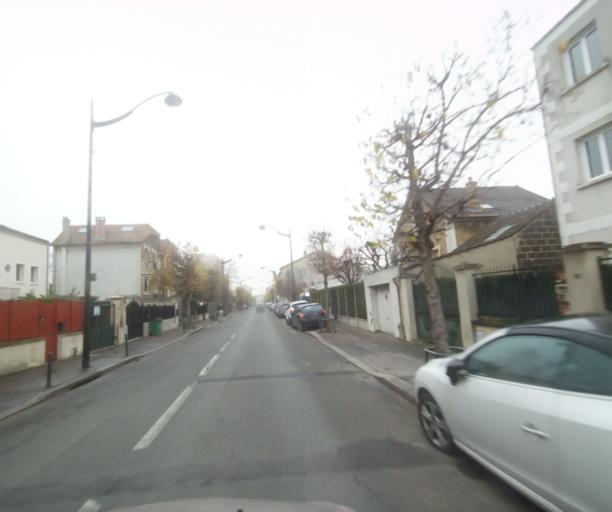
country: FR
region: Ile-de-France
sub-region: Departement de Seine-Saint-Denis
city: Les Pavillons-sous-Bois
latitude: 48.9062
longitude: 2.4998
